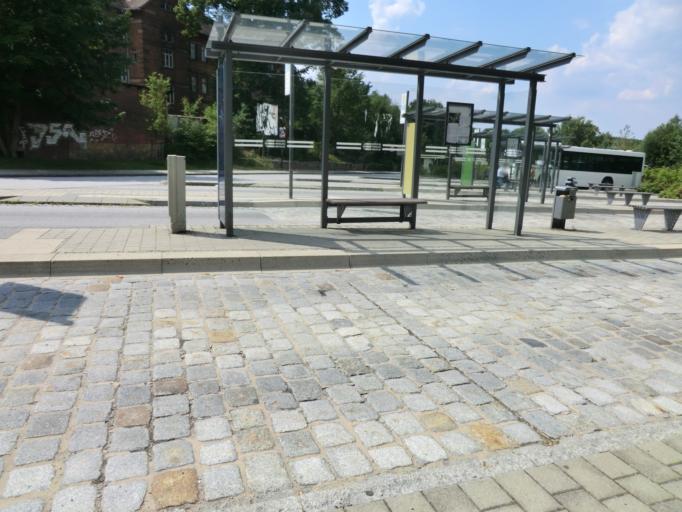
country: DE
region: Saxony
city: Radeberg
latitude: 51.1126
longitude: 13.9124
